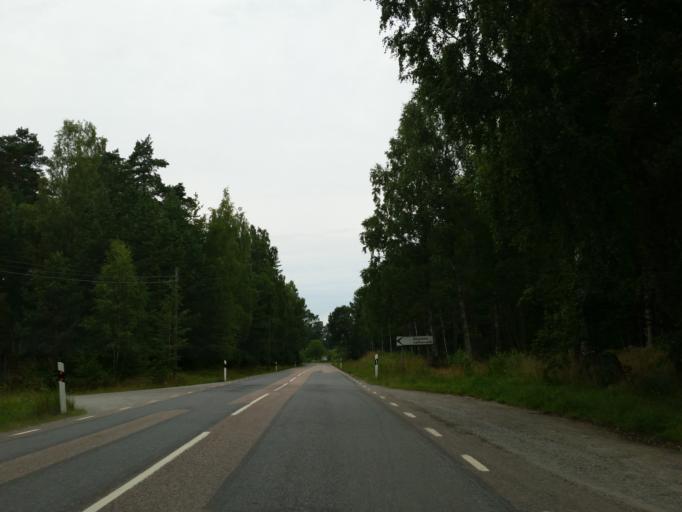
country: SE
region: Stockholm
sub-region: Sodertalje Kommun
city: Soedertaelje
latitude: 59.2007
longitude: 17.5716
